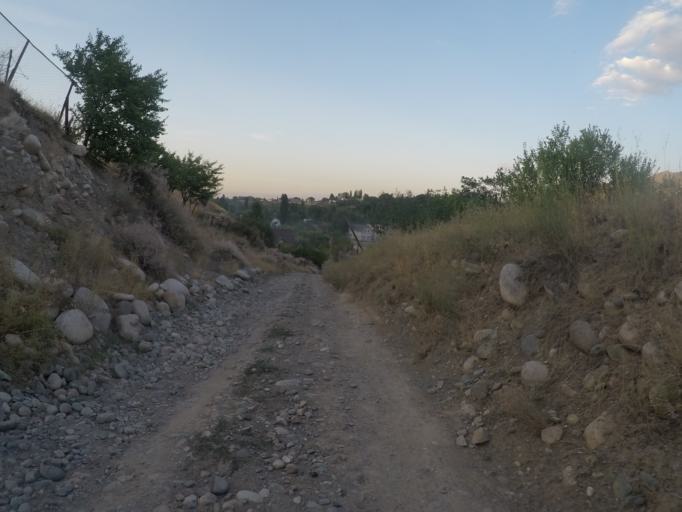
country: KG
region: Chuy
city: Bishkek
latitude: 42.7734
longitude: 74.6403
